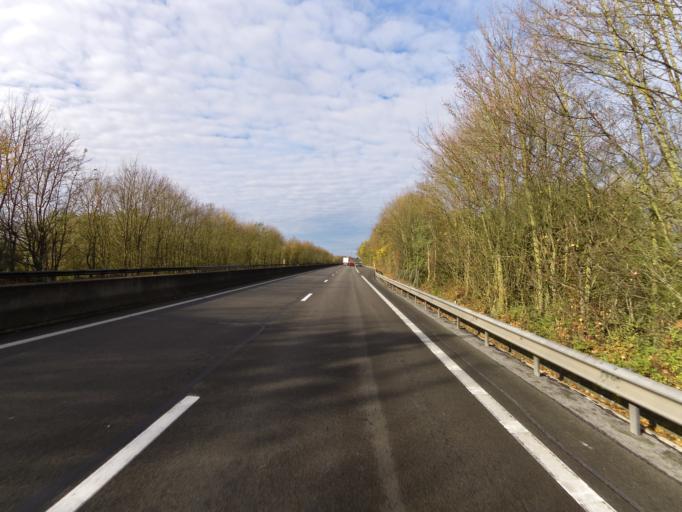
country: FR
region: Picardie
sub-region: Departement de l'Aisne
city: Itancourt
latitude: 49.7563
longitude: 3.3737
